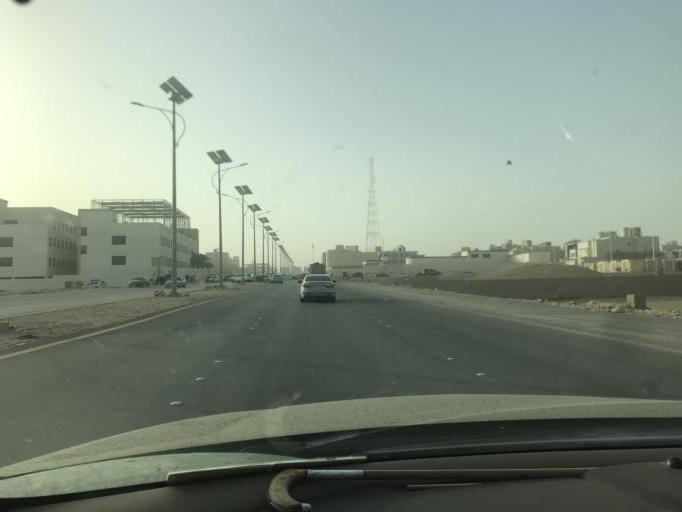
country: SA
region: Ar Riyad
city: Riyadh
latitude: 24.8437
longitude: 46.6652
